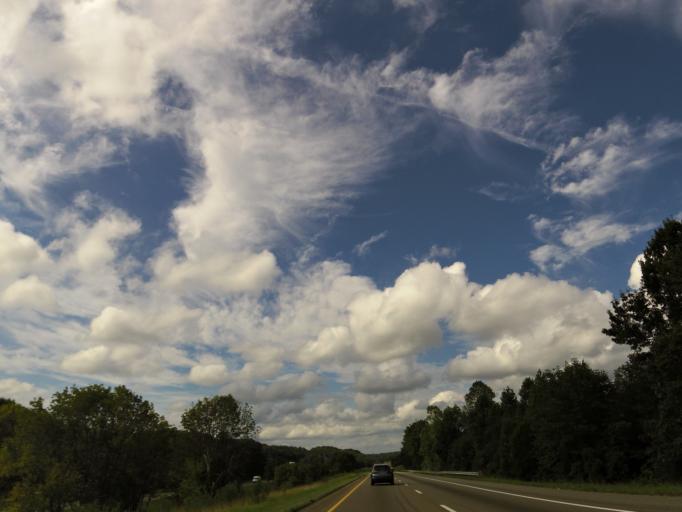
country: US
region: Tennessee
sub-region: Loudon County
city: Loudon
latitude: 35.7751
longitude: -84.3532
